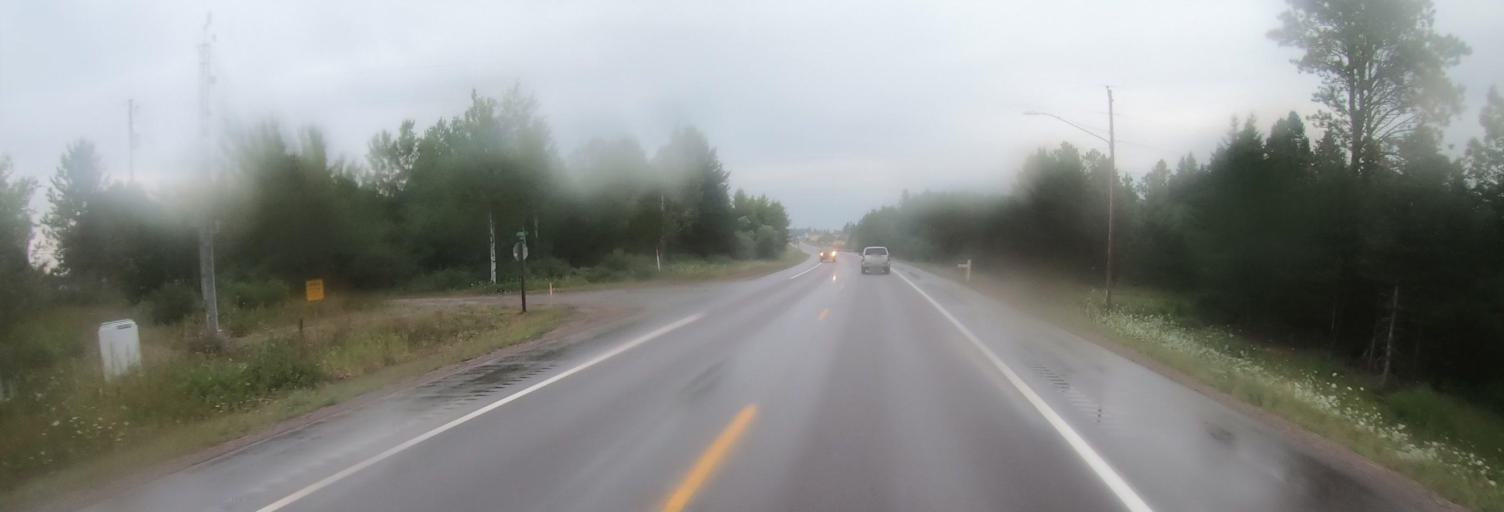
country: US
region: Michigan
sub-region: Houghton County
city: Laurium
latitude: 47.2190
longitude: -88.4576
